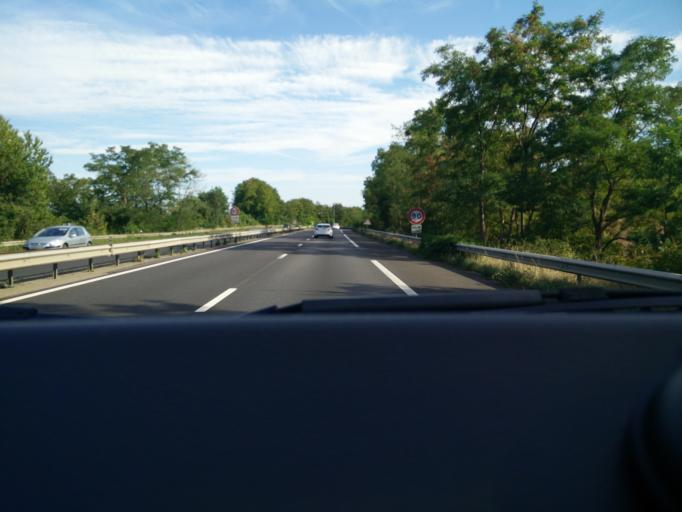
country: FR
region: Lorraine
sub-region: Departement de Meurthe-et-Moselle
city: Rosieres-aux-Salines
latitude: 48.6125
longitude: 6.3285
